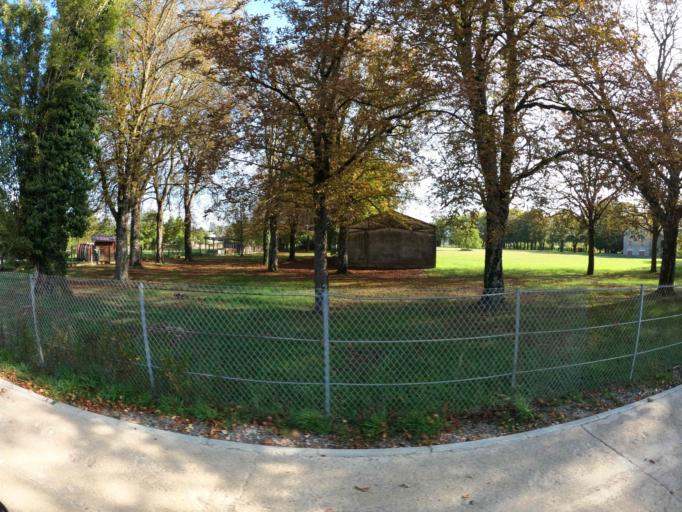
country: FR
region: Franche-Comte
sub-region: Departement du Jura
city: Bletterans
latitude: 46.7413
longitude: 5.4980
